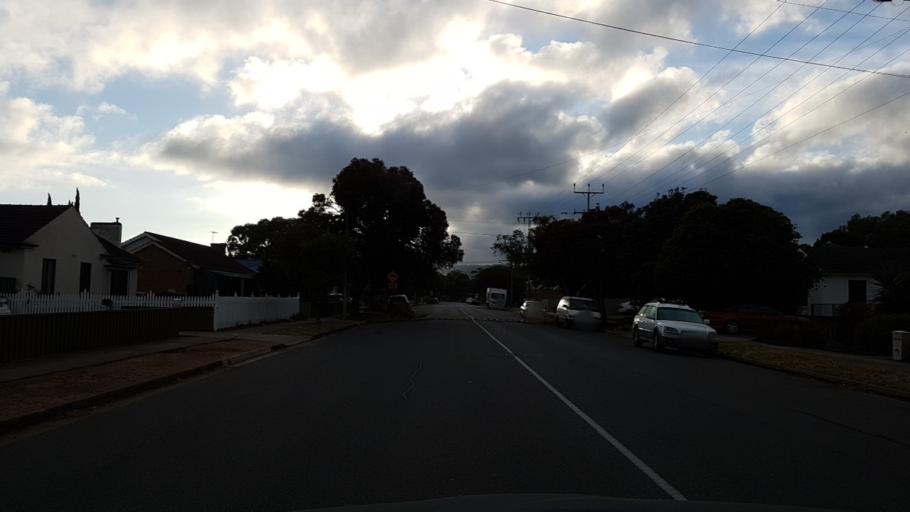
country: AU
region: South Australia
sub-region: Marion
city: Sturt
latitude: -35.0022
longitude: 138.5548
